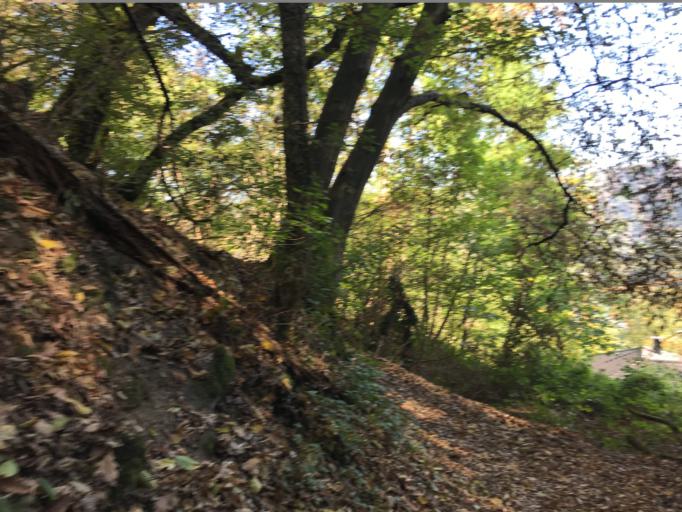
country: DE
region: Rheinland-Pfalz
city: Kobern-Gondorf
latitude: 50.3002
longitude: 7.4558
